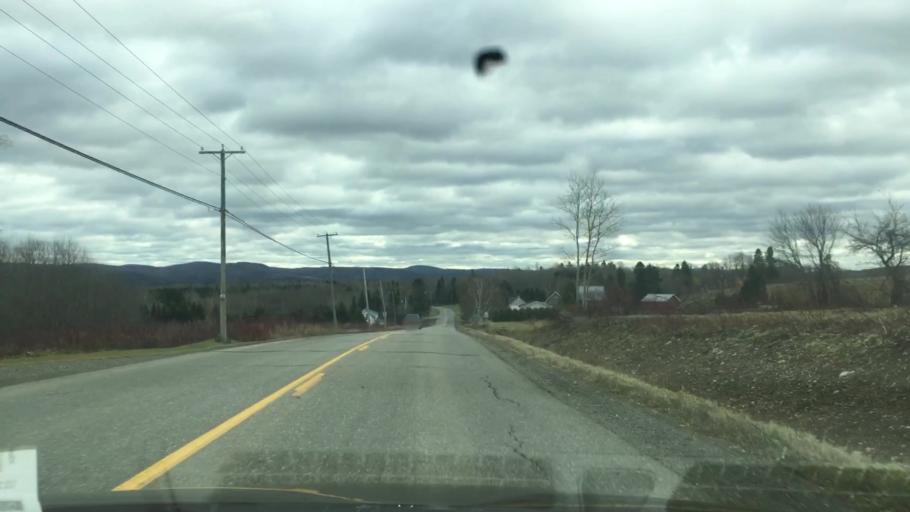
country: US
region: Maine
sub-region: Aroostook County
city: Fort Fairfield
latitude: 46.7538
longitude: -67.7597
